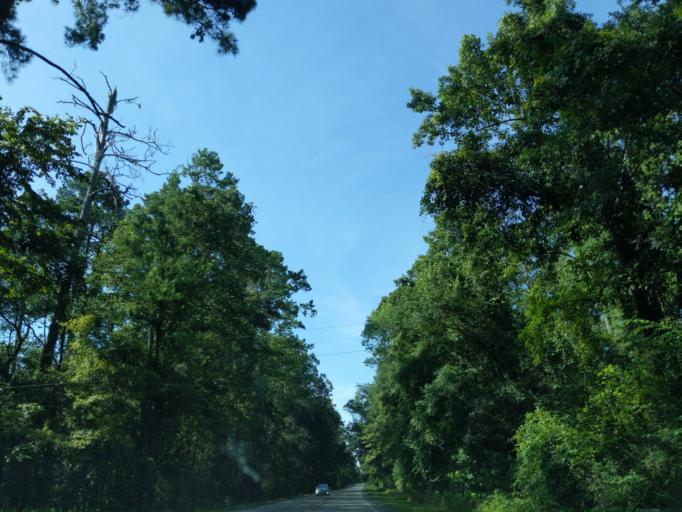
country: US
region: Florida
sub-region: Wakulla County
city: Crawfordville
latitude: 30.2465
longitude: -84.3130
